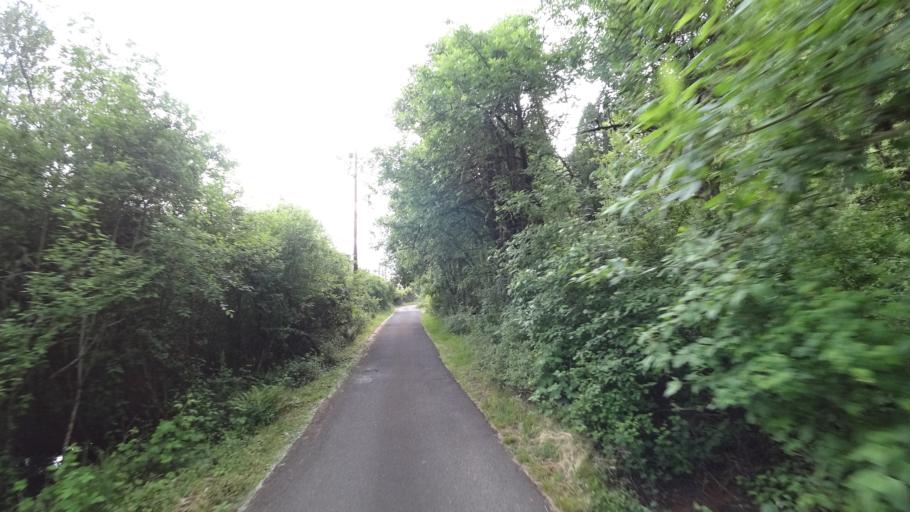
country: US
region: Oregon
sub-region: Clackamas County
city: Happy Valley
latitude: 45.4790
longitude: -122.5049
